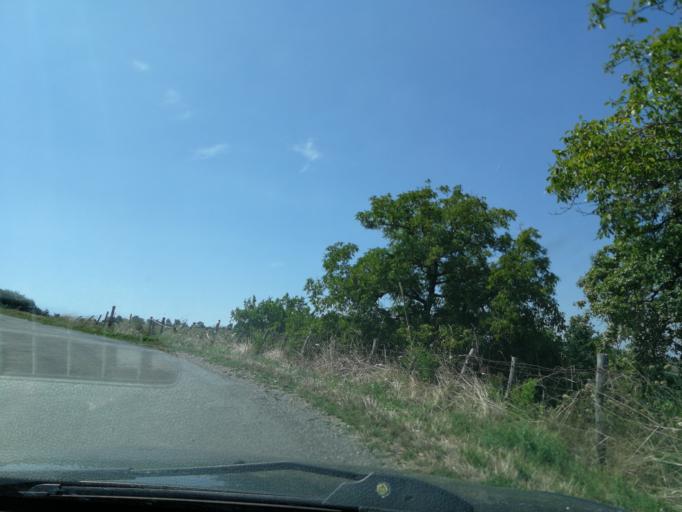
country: FR
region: Auvergne
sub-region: Departement du Cantal
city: Maurs
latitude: 44.6822
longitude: 2.3237
